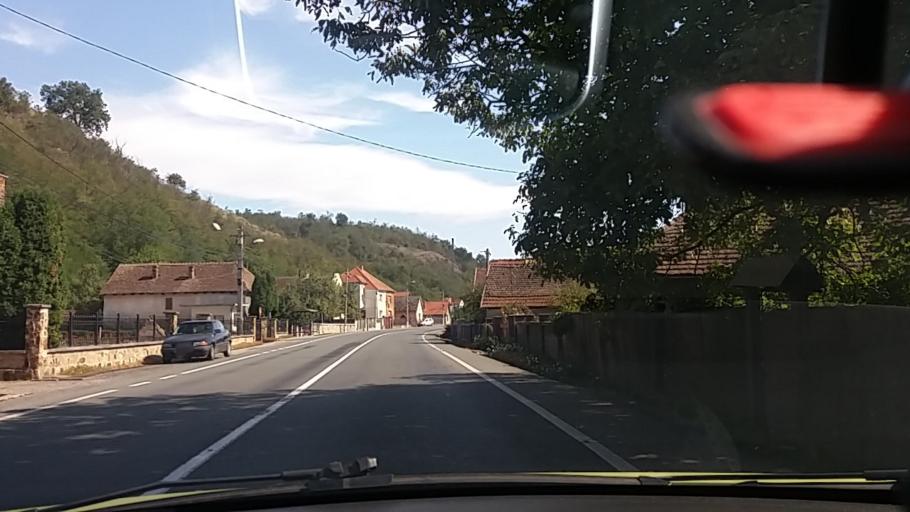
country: RO
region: Arad
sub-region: Oras Lipova
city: Lipova
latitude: 46.1031
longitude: 21.7018
